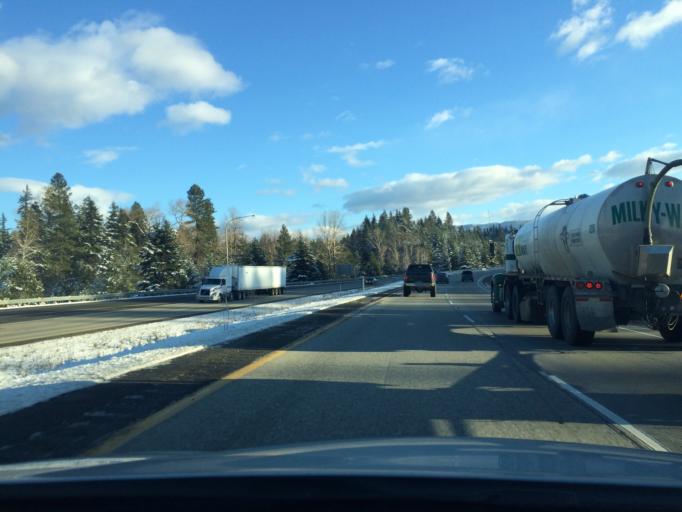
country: US
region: Washington
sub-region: Kittitas County
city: Cle Elum
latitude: 47.1938
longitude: -121.0499
